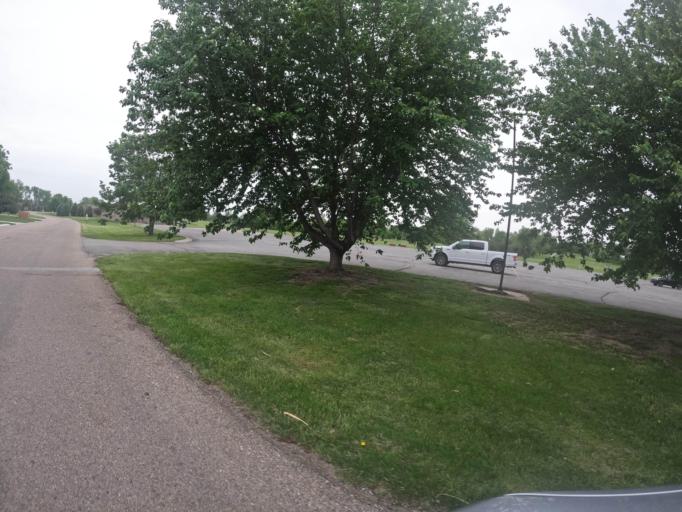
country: US
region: Nebraska
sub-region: Sarpy County
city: Offutt Air Force Base
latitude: 41.0507
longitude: -95.9604
